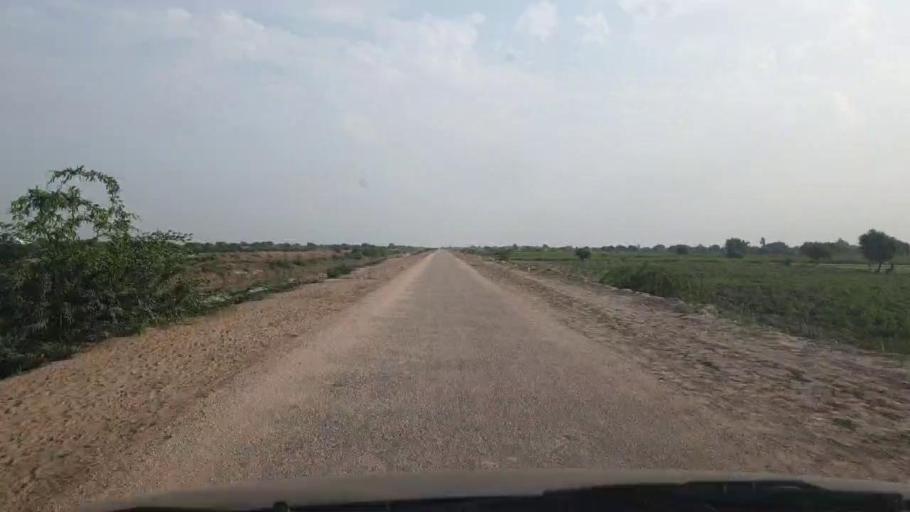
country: PK
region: Sindh
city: Badin
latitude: 24.5446
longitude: 68.6726
